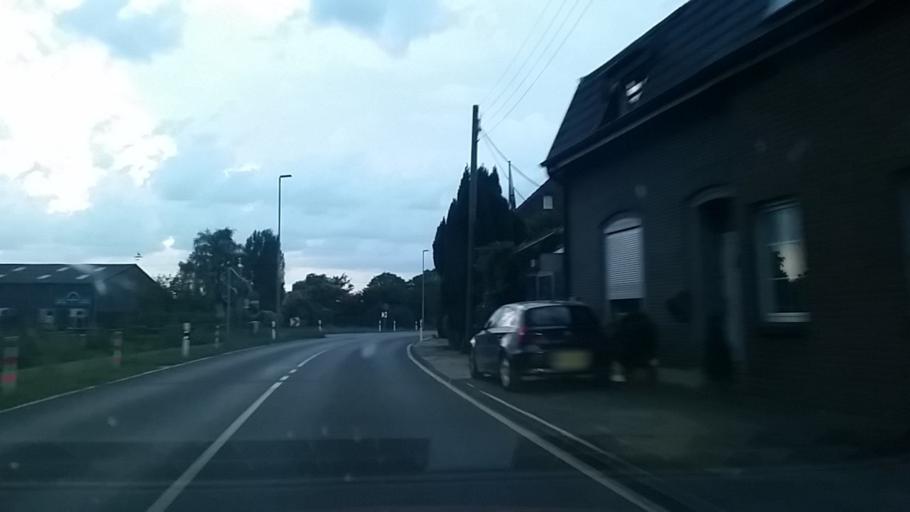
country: DE
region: North Rhine-Westphalia
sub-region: Regierungsbezirk Dusseldorf
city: Kaarst
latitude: 51.2524
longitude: 6.5885
